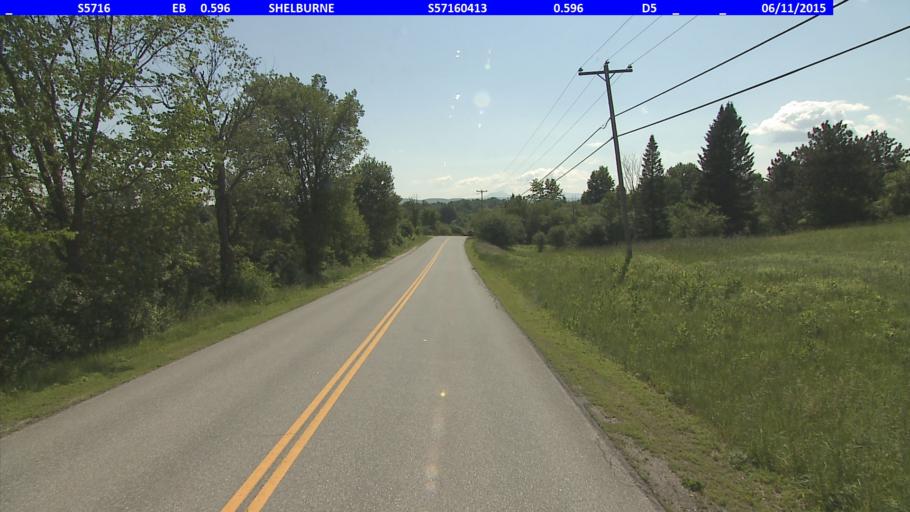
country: US
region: Vermont
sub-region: Chittenden County
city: South Burlington
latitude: 44.3736
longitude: -73.2001
